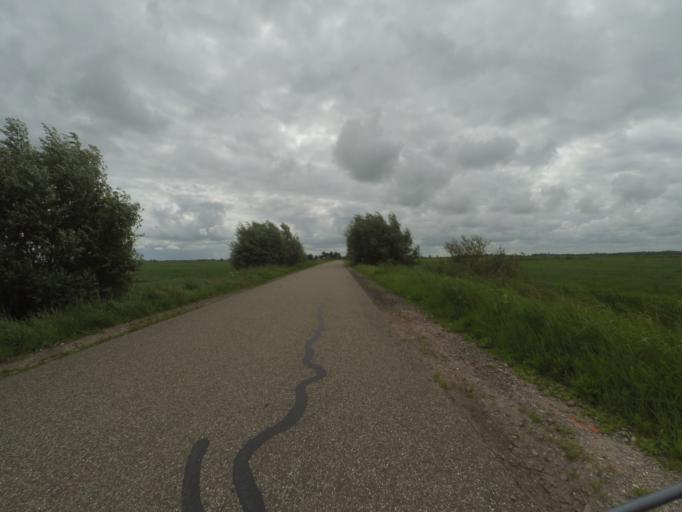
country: NL
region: Friesland
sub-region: Gemeente Kollumerland en Nieuwkruisland
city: Kollumerzwaag
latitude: 53.3135
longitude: 6.0896
